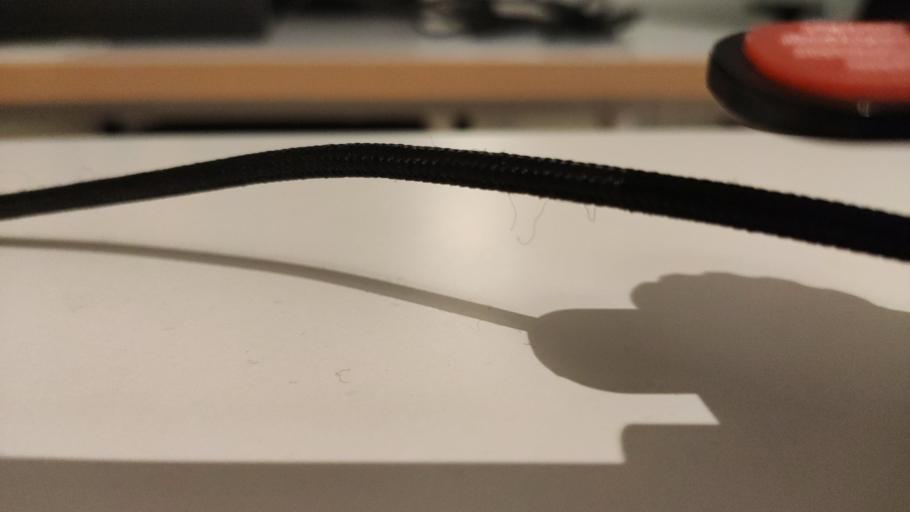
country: RU
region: Moskovskaya
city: Novosin'kovo
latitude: 56.3979
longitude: 37.2665
